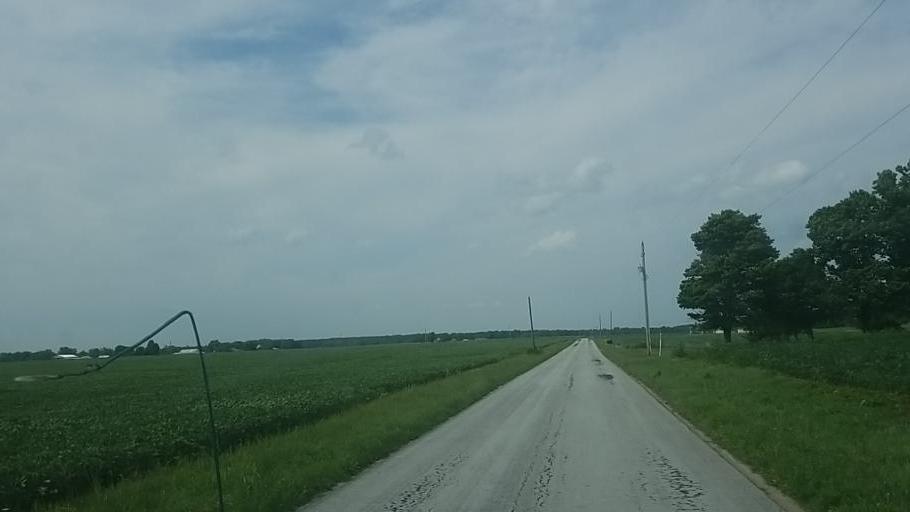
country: US
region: Ohio
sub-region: Hardin County
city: Forest
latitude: 40.7760
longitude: -83.5572
